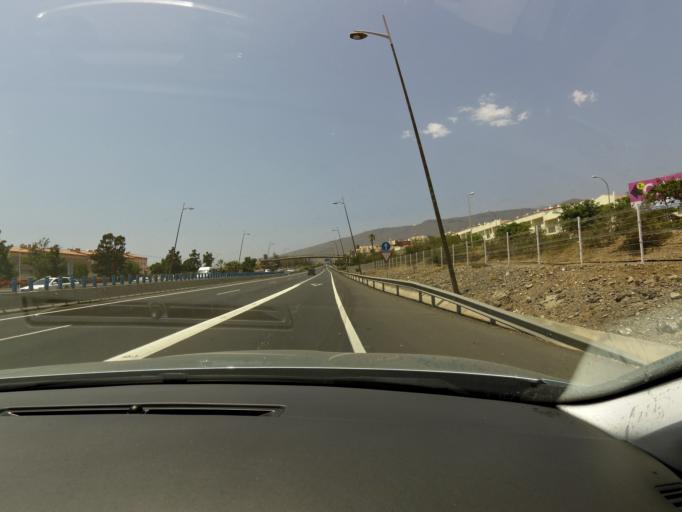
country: ES
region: Canary Islands
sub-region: Provincia de Santa Cruz de Tenerife
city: Playa de las Americas
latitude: 28.0908
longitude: -16.7292
